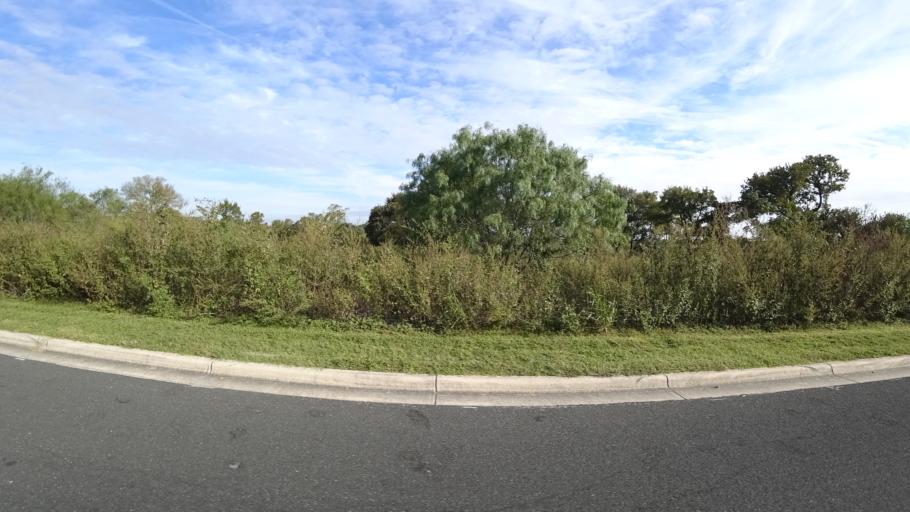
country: US
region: Texas
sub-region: Travis County
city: Austin
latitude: 30.2006
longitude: -97.7305
